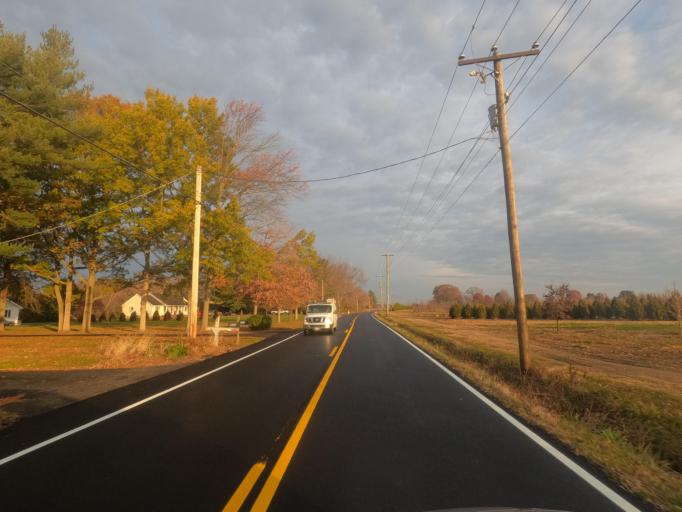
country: US
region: Delaware
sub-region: New Castle County
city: Townsend
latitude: 39.2765
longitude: -75.8379
